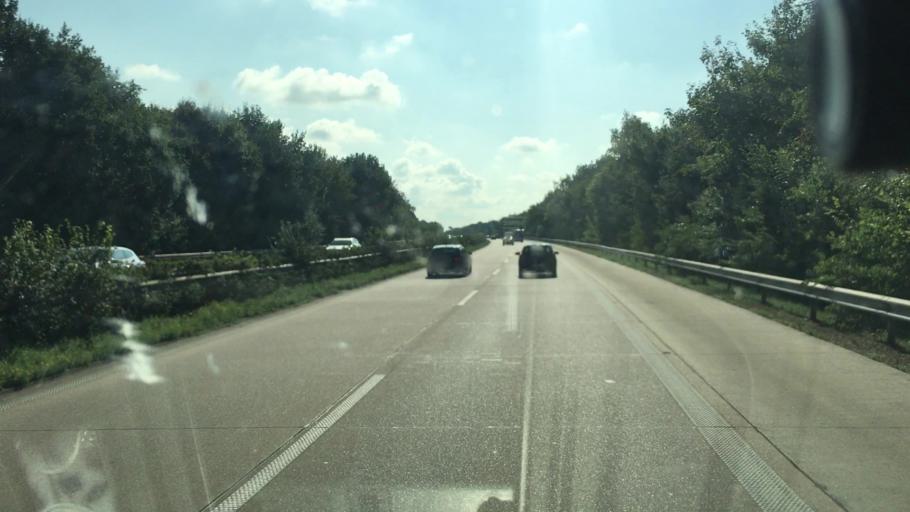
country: DE
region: Lower Saxony
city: Rastede
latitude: 53.2304
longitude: 8.1871
